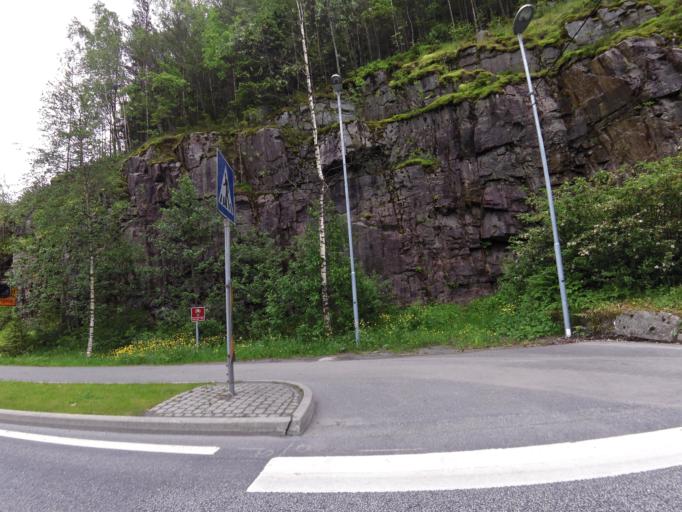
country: NO
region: Vest-Agder
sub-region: Flekkefjord
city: Flekkefjord
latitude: 58.2983
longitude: 6.6753
